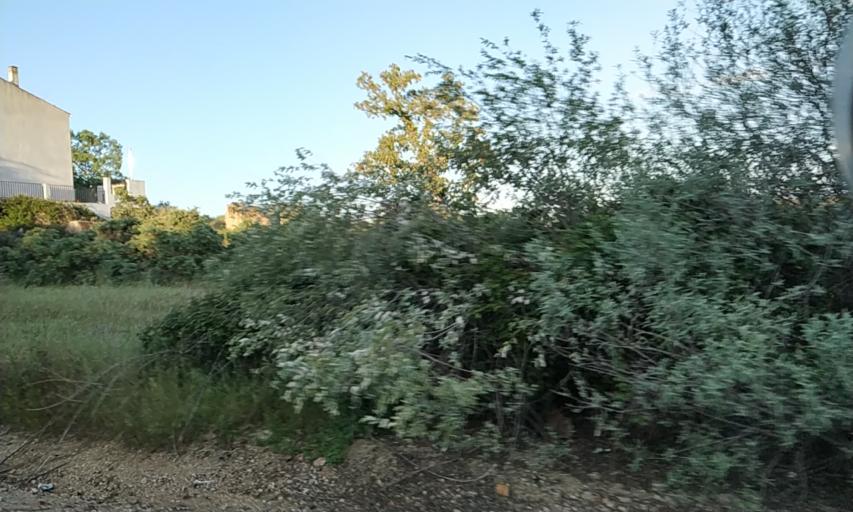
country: ES
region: Extremadura
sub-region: Provincia de Caceres
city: Valencia de Alcantara
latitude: 39.4026
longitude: -7.2505
